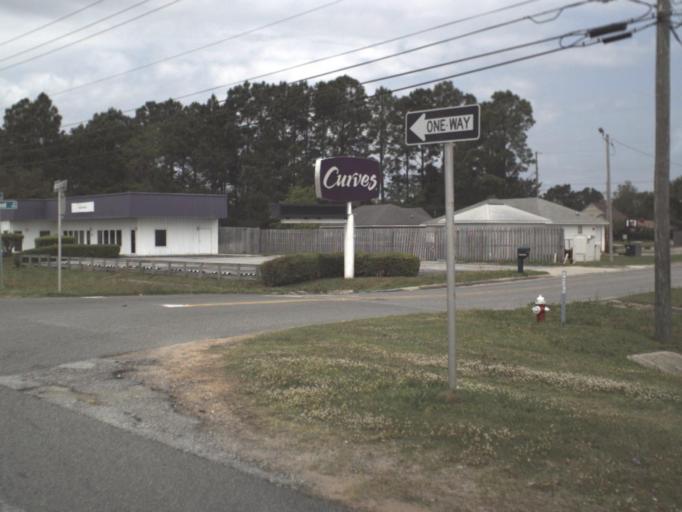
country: US
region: Florida
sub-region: Escambia County
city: Myrtle Grove
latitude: 30.3977
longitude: -87.3041
